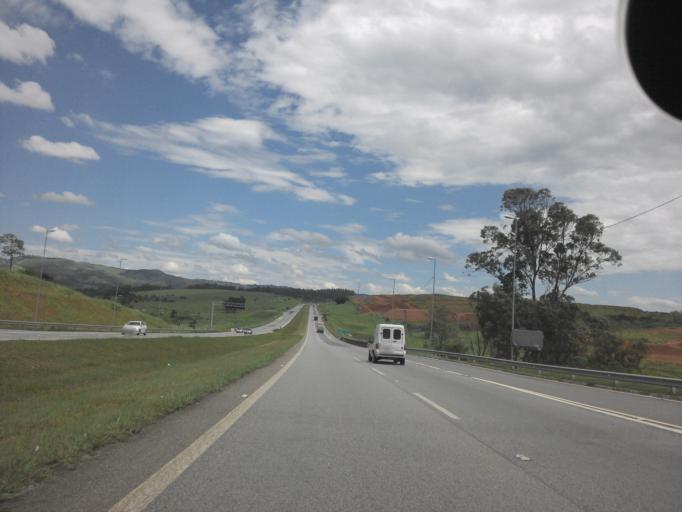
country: BR
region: Sao Paulo
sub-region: Cacapava
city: Cacapava
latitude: -23.1189
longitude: -45.6536
